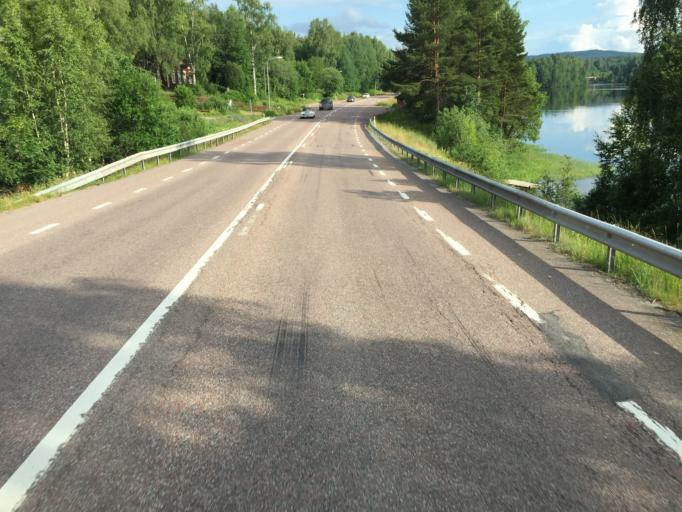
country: SE
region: Dalarna
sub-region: Gagnefs Kommun
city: Djuras
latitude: 60.5458
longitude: 15.2773
